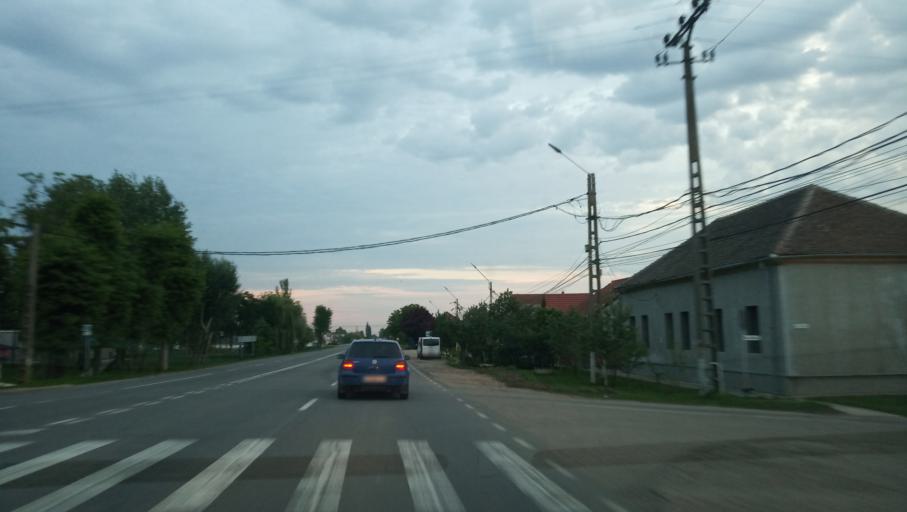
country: RO
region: Timis
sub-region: Comuna Sag
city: Sag
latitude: 45.6491
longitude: 21.1747
